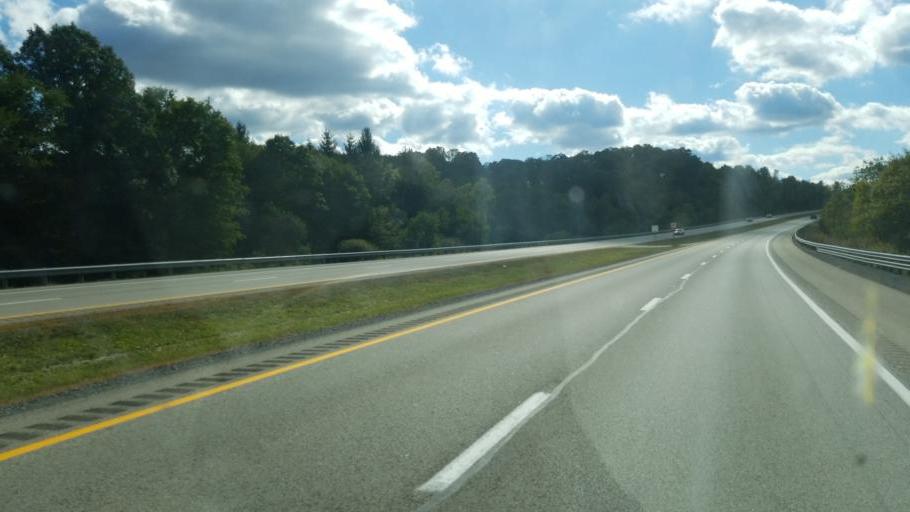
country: US
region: West Virginia
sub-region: Monongalia County
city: Cheat Lake
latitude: 39.6586
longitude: -79.6822
